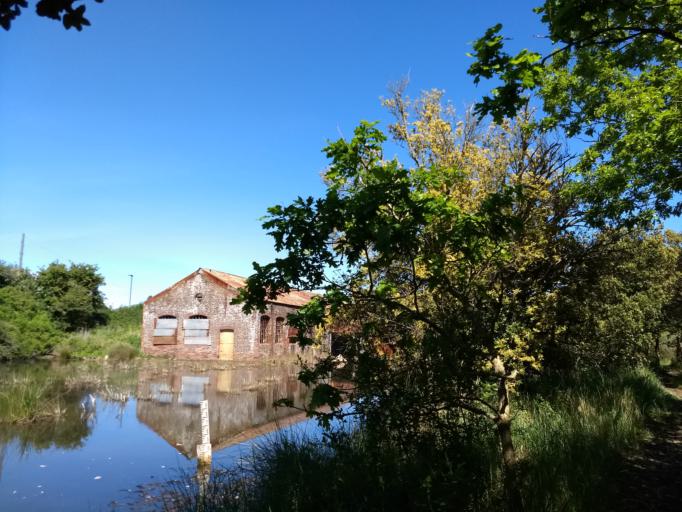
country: GB
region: England
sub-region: Isle of Wight
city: Bembridge
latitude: 50.6898
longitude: -1.0988
